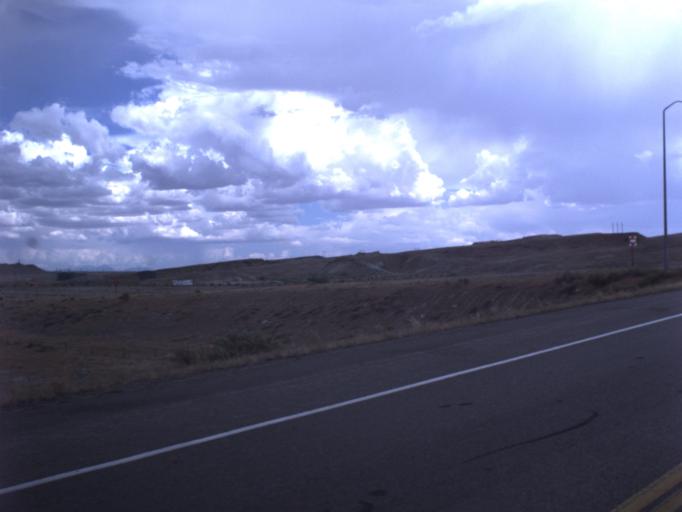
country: US
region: Utah
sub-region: Carbon County
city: East Carbon City
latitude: 38.9774
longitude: -110.1213
